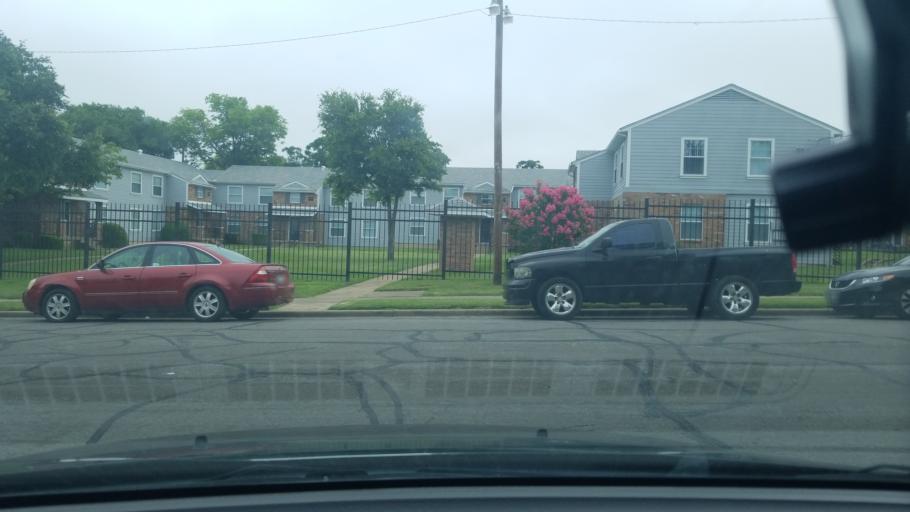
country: US
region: Texas
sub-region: Dallas County
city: Balch Springs
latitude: 32.7546
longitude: -96.6926
